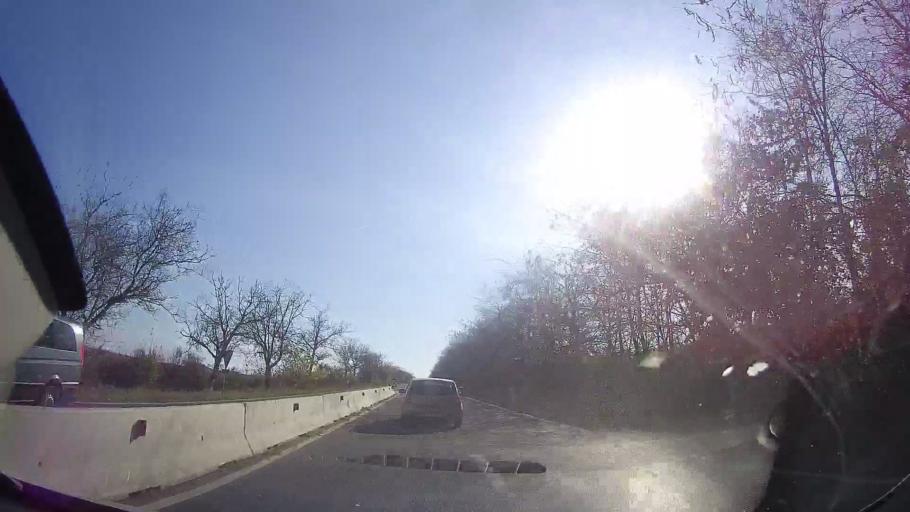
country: RO
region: Constanta
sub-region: Comuna Douazeci si Trei August
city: Douazeci si Trei August
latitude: 43.8955
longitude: 28.5716
